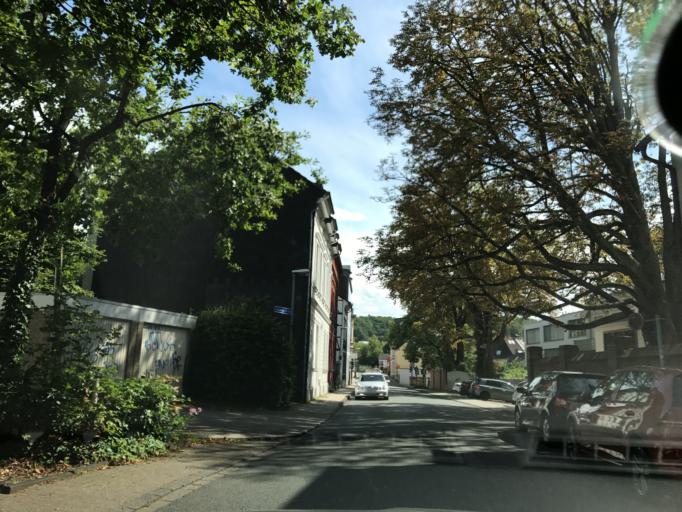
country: DE
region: North Rhine-Westphalia
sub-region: Regierungsbezirk Dusseldorf
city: Essen
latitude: 51.3916
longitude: 7.0037
